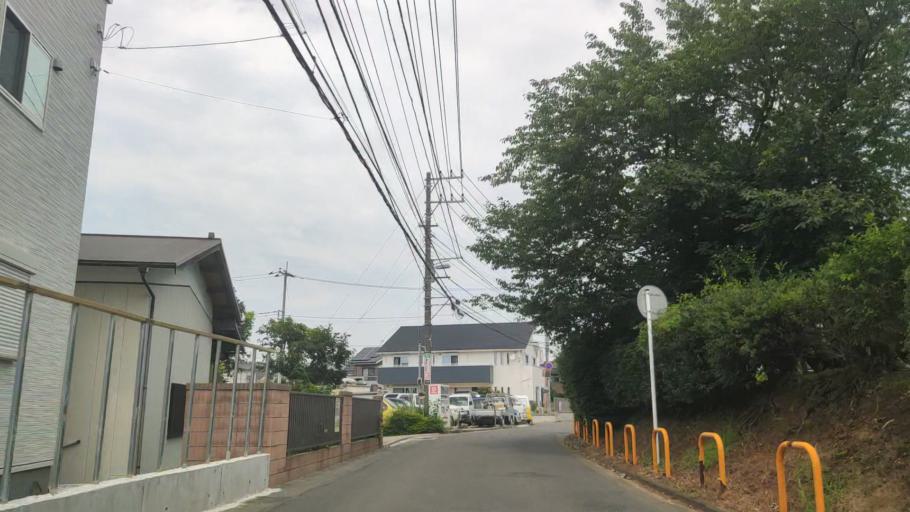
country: JP
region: Kanagawa
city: Atsugi
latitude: 35.4267
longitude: 139.3966
